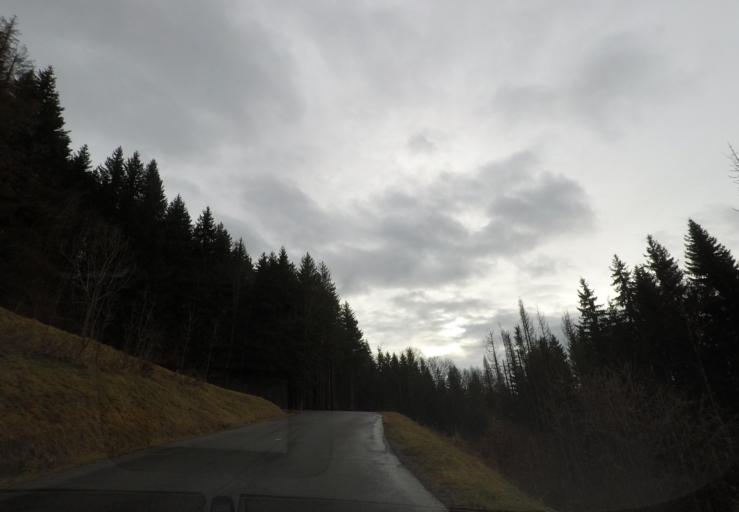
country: FR
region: Rhone-Alpes
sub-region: Departement de la Haute-Savoie
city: Chatillon-sur-Cluses
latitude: 46.0798
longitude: 6.6155
